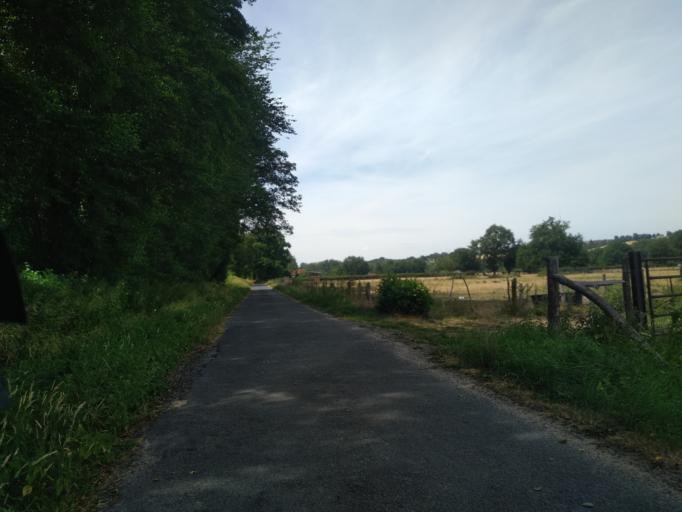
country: FR
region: Auvergne
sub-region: Departement de l'Allier
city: Diou
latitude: 46.5294
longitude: 3.7714
